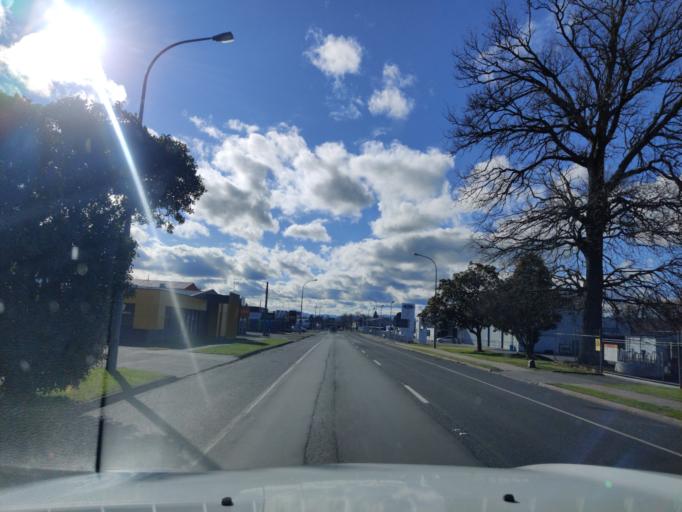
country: NZ
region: Waikato
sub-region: Matamata-Piako District
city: Matamata
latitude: -37.8129
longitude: 175.7706
